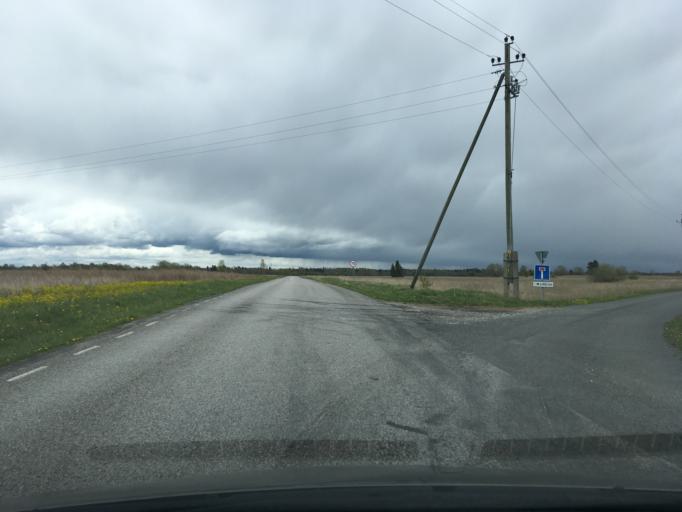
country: EE
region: Harju
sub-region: Rae vald
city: Vaida
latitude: 59.3577
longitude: 24.9774
